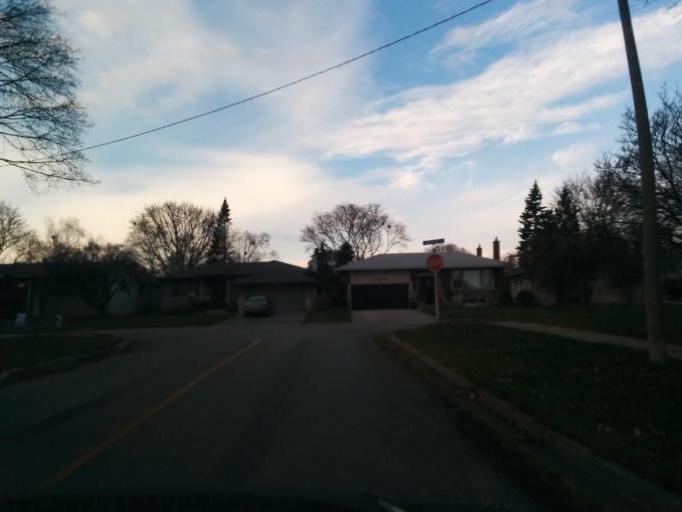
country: CA
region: Ontario
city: Etobicoke
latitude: 43.6841
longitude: -79.5424
